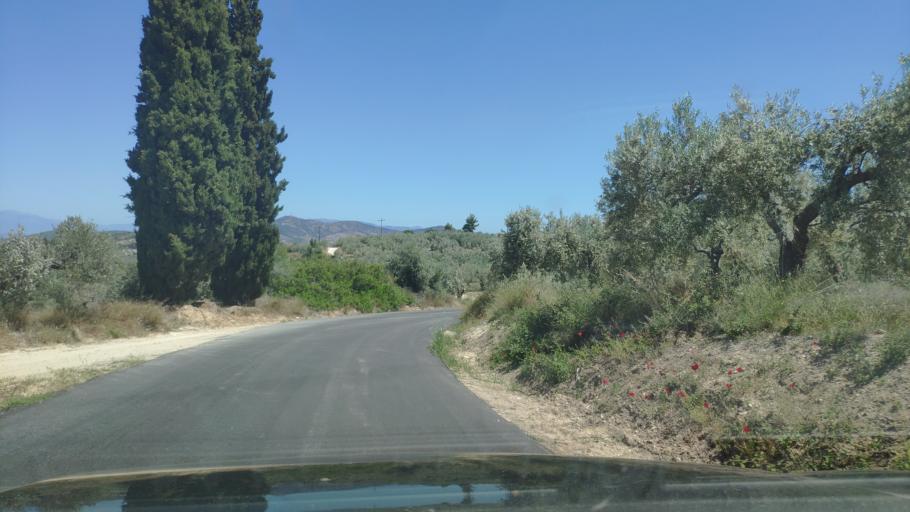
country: GR
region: Peloponnese
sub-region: Nomos Korinthias
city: Athikia
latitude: 37.8050
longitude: 22.9042
